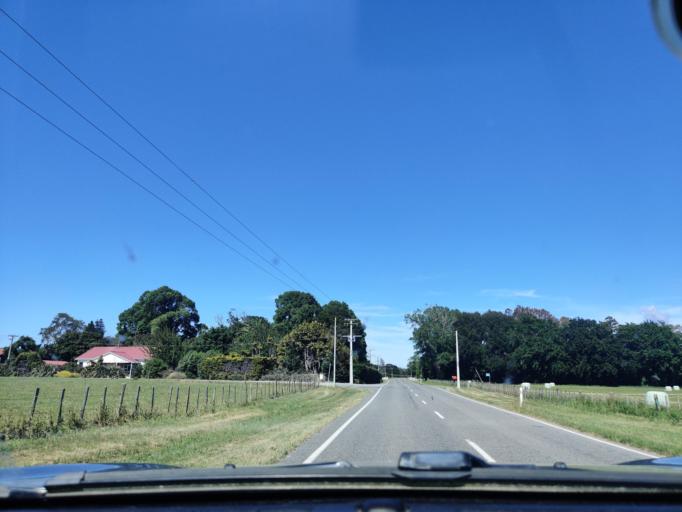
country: NZ
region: Wellington
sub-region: South Wairarapa District
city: Waipawa
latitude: -41.3167
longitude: 175.2586
